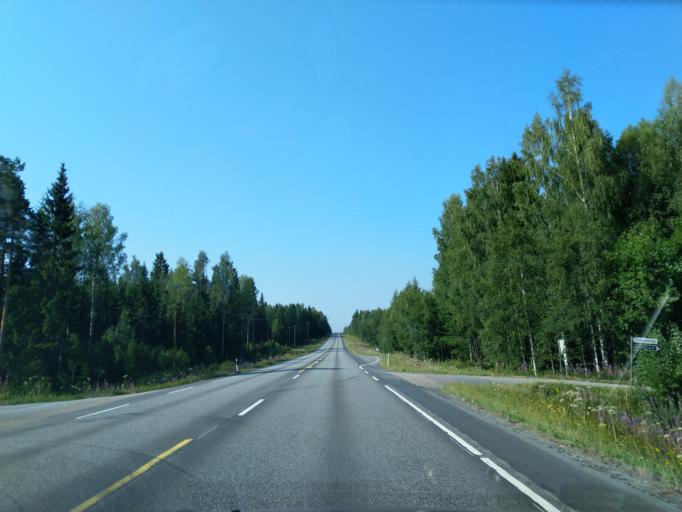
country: FI
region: Satakunta
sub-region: Pori
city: Pomarkku
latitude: 61.7279
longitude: 22.0669
